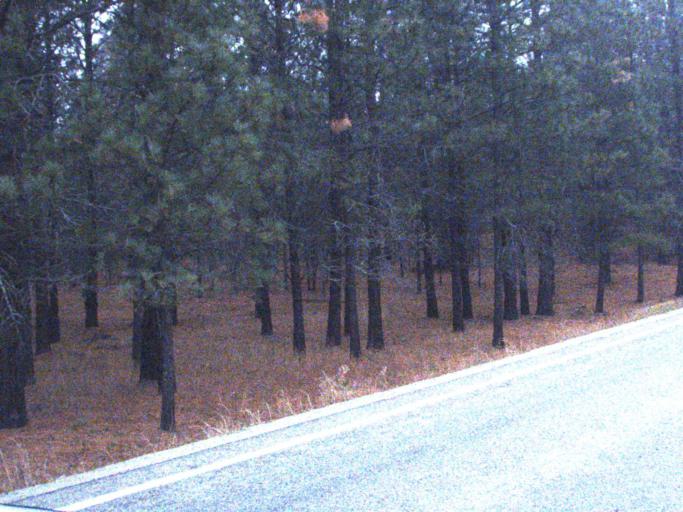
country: CA
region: British Columbia
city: Grand Forks
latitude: 48.9958
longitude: -118.2250
